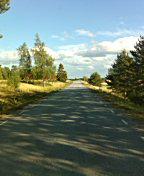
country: SE
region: Uppsala
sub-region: Enkopings Kommun
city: Grillby
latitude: 59.6704
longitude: 17.2255
